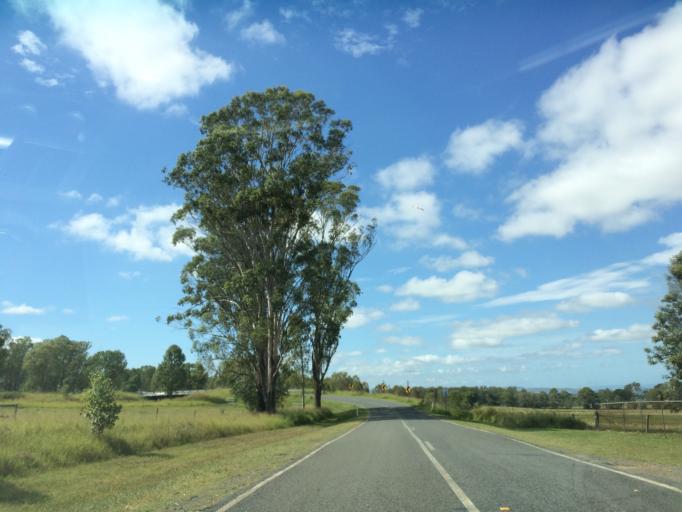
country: AU
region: Queensland
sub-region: Logan
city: Cedar Vale
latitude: -27.8874
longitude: 152.9727
